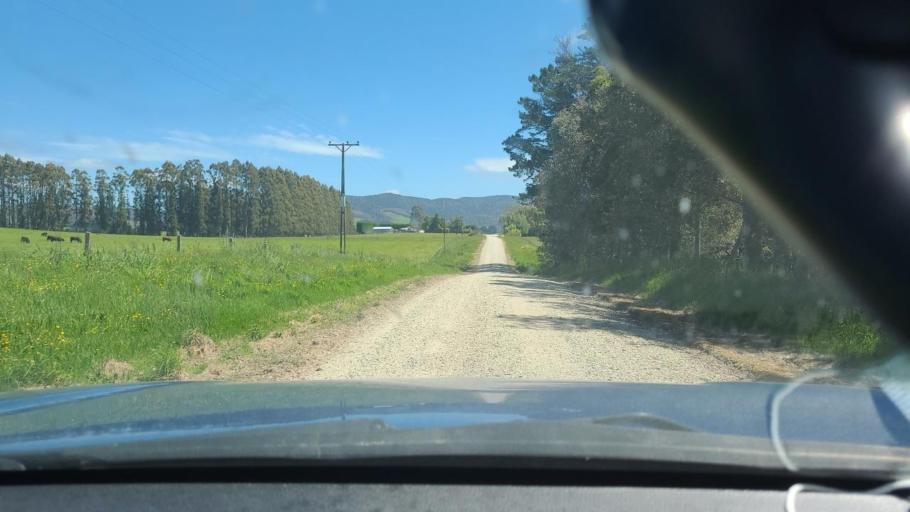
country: NZ
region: Southland
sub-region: Gore District
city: Gore
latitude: -46.4230
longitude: 169.0584
